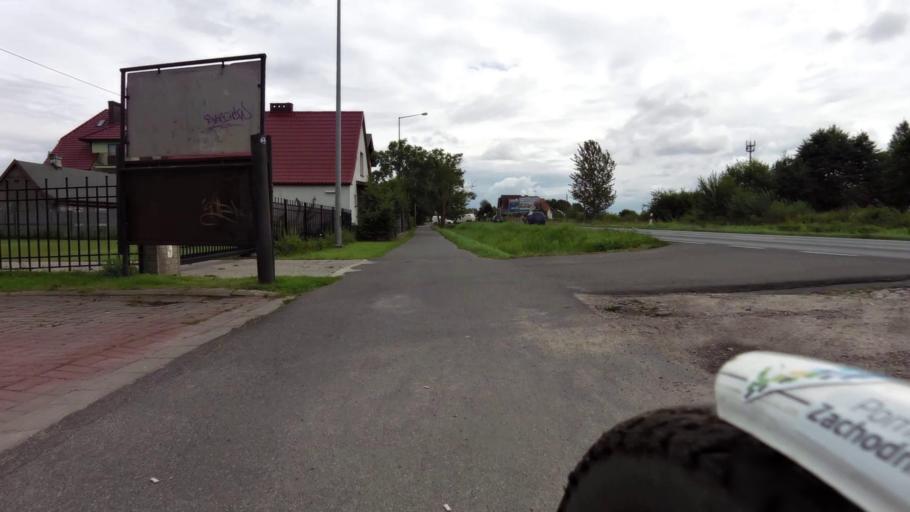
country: PL
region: West Pomeranian Voivodeship
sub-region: Powiat koszalinski
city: Mielno
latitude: 54.2529
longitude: 16.0566
